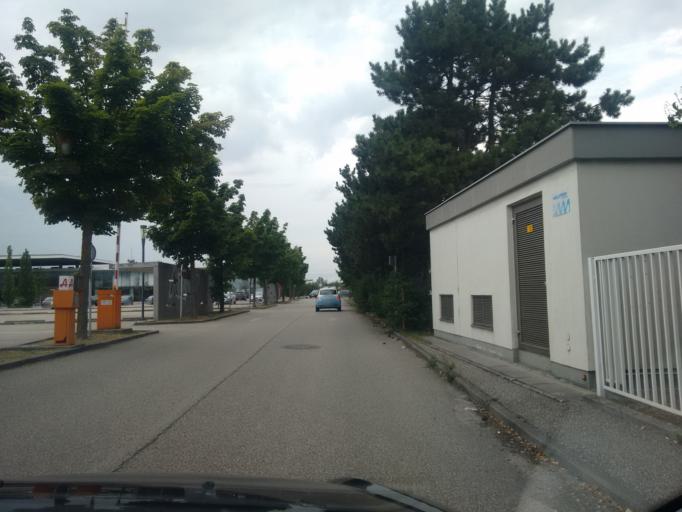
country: AT
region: Upper Austria
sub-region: Wels Stadt
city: Wels
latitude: 48.1804
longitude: 14.0639
